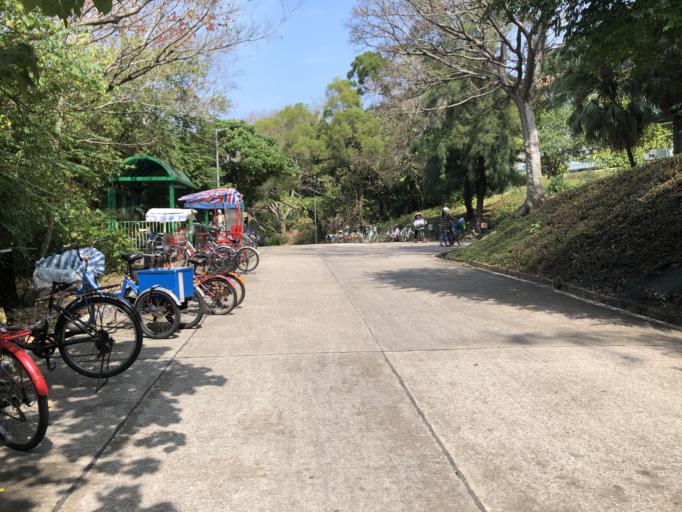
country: HK
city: Yung Shue Wan
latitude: 22.2126
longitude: 114.0241
